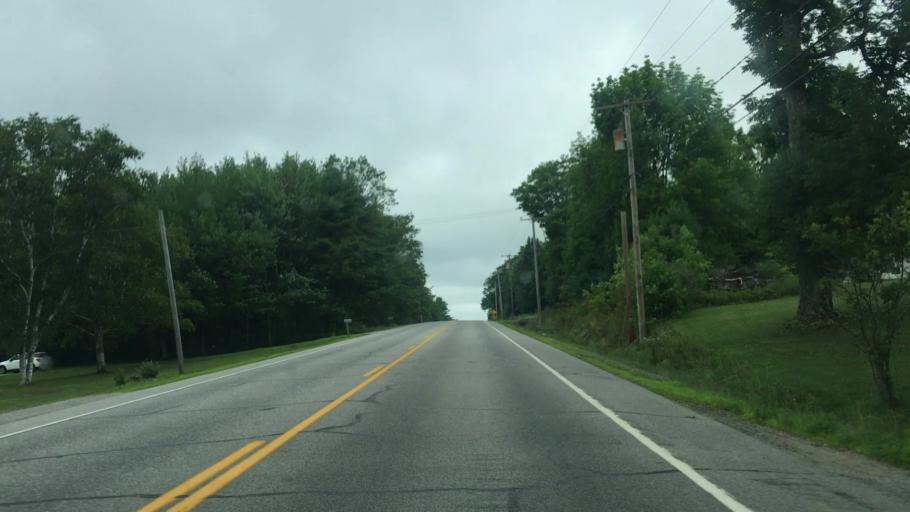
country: US
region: Maine
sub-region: Sagadahoc County
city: Richmond
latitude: 44.1432
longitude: -69.7425
